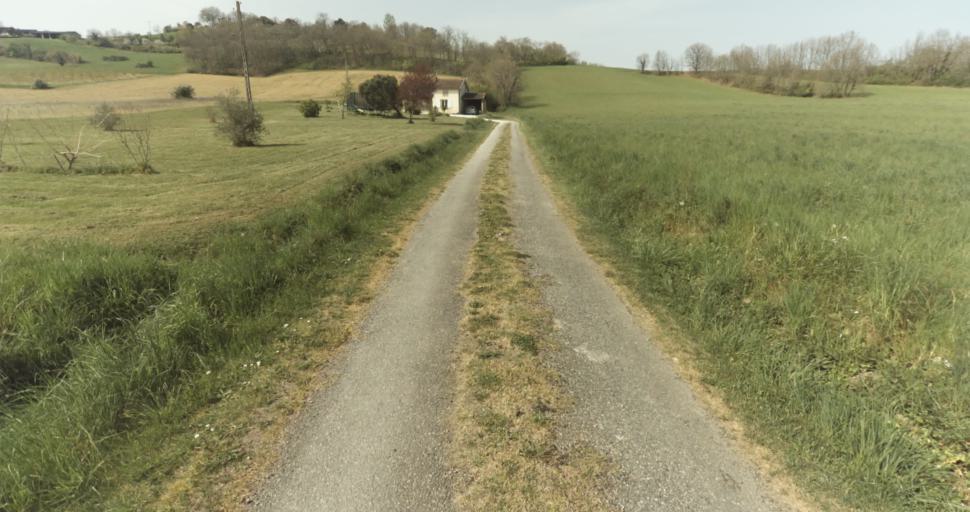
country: FR
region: Midi-Pyrenees
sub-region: Departement du Tarn-et-Garonne
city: Moissac
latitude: 44.1297
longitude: 1.1543
